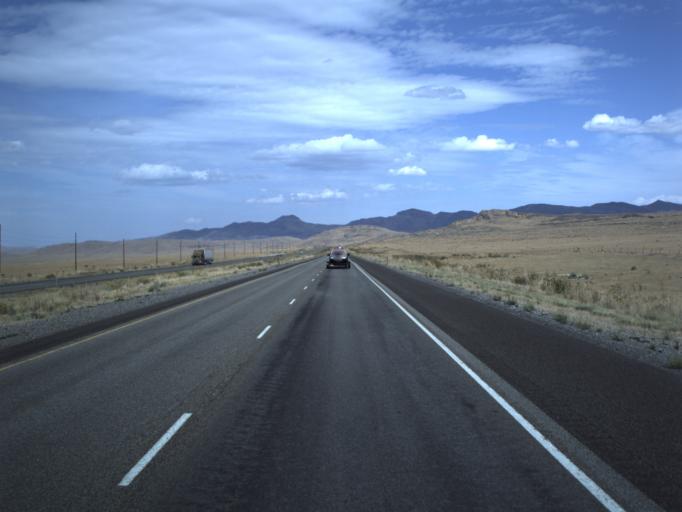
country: US
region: Utah
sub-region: Tooele County
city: Grantsville
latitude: 40.7885
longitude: -112.9577
